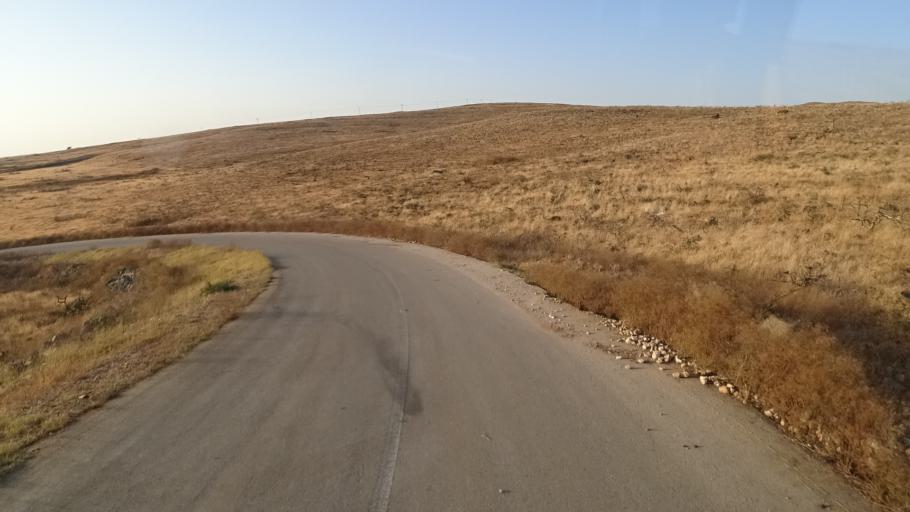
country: OM
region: Zufar
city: Salalah
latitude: 17.1546
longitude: 54.6219
